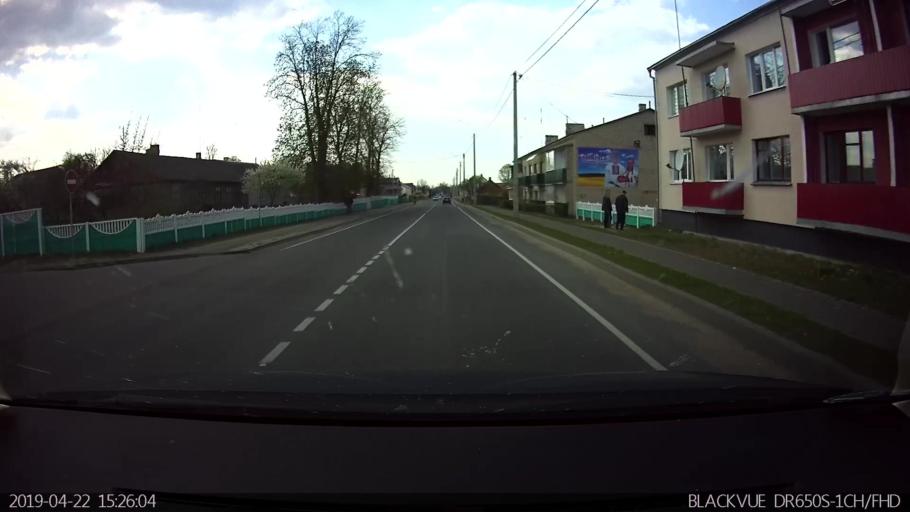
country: BY
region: Brest
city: Vysokaye
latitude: 52.3667
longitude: 23.3870
